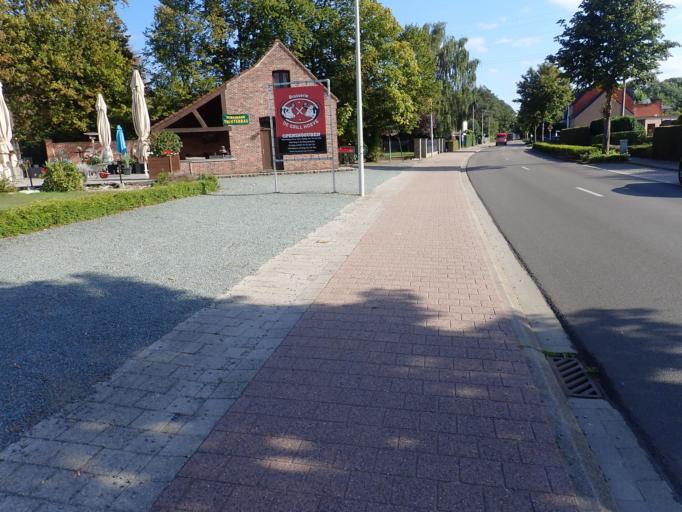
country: BE
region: Flanders
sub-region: Provincie Antwerpen
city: Nijlen
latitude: 51.1504
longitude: 4.6764
